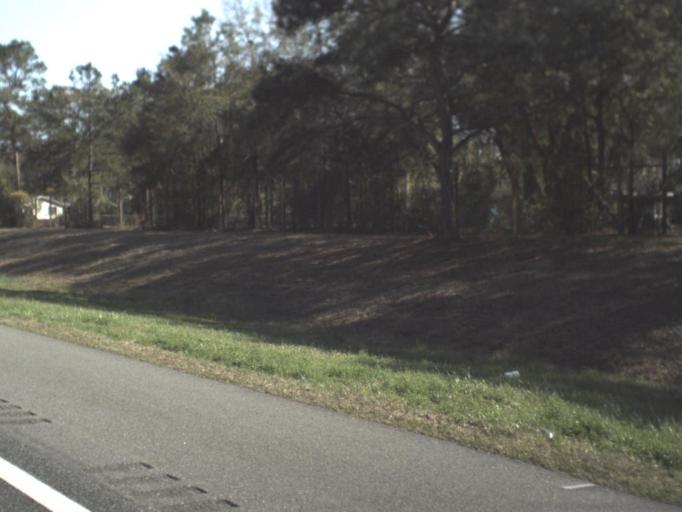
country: US
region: Florida
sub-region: Gadsden County
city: Midway
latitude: 30.5056
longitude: -84.4618
